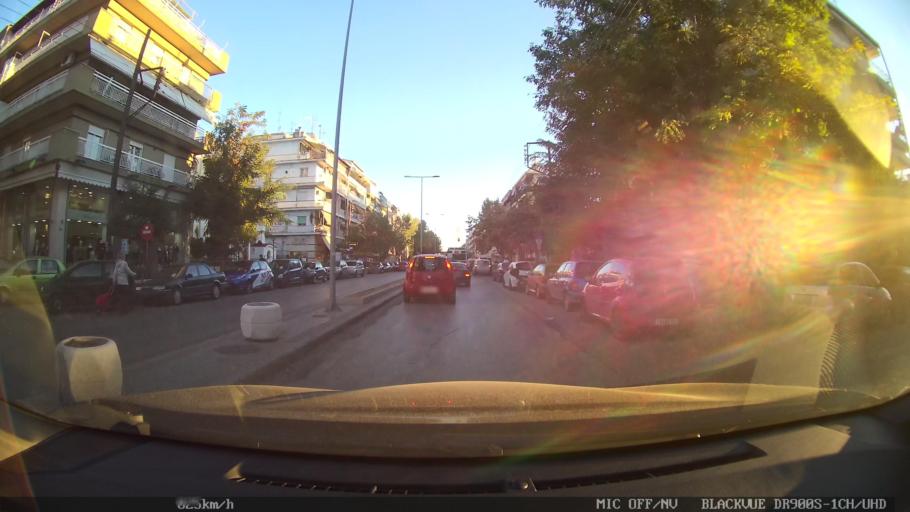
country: GR
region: Central Macedonia
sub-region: Nomos Thessalonikis
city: Triandria
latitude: 40.6044
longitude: 22.9687
